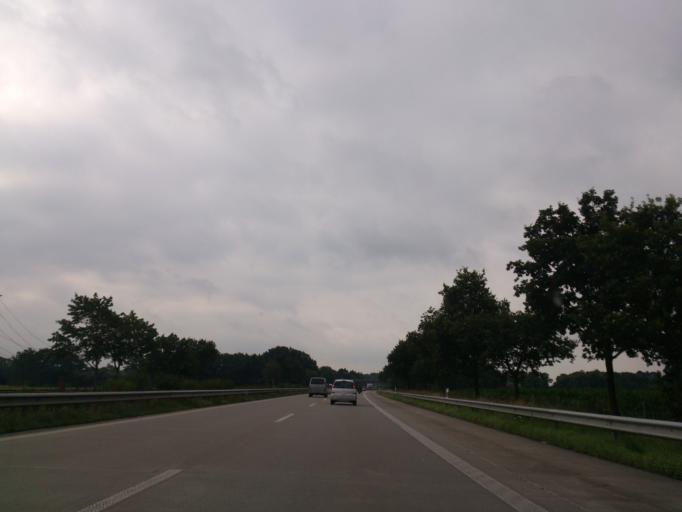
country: DE
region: Schleswig-Holstein
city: Klein Offenseth-Sparrieshoop
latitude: 53.7822
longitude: 9.7042
